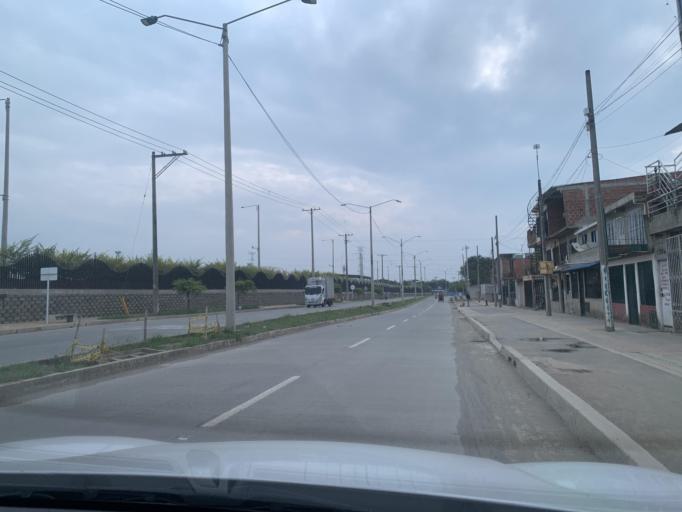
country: CO
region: Valle del Cauca
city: Cali
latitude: 3.4105
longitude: -76.4770
